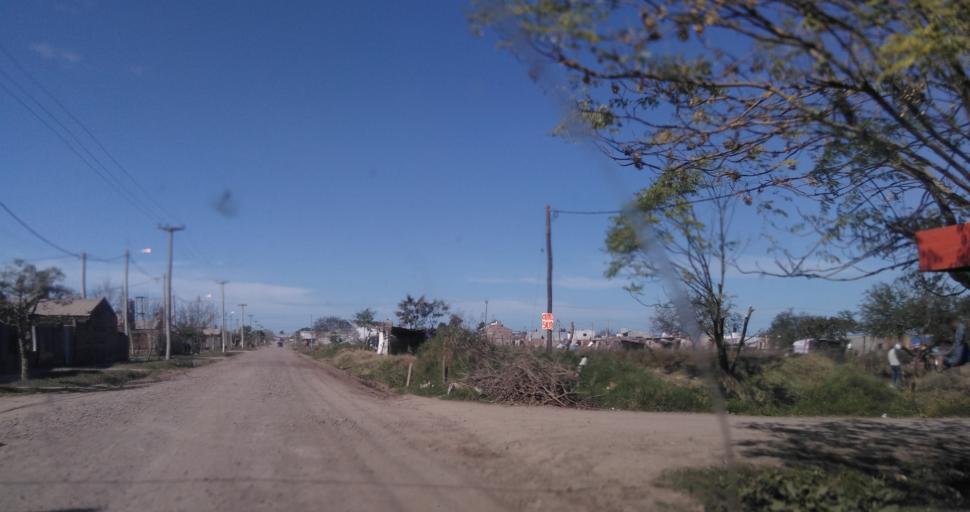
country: AR
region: Chaco
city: Fontana
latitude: -27.4564
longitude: -59.0461
